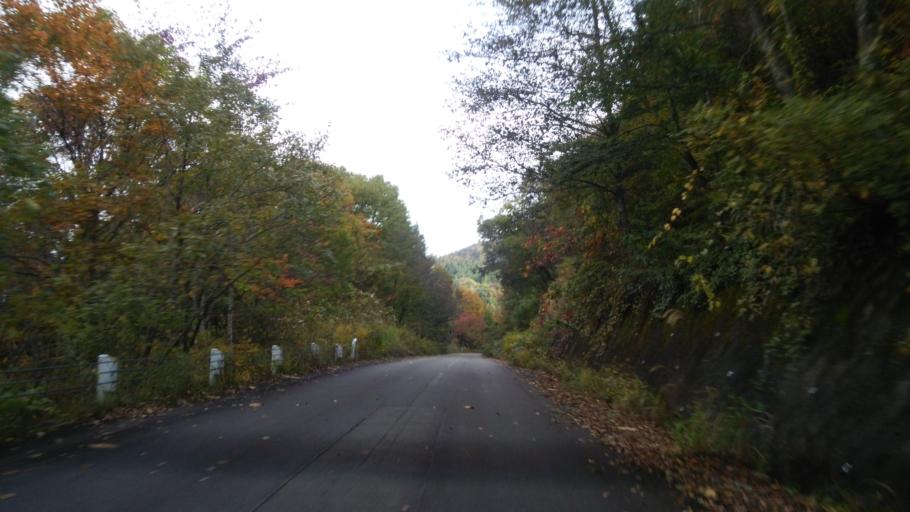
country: JP
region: Fukushima
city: Kitakata
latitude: 37.3976
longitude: 139.7396
